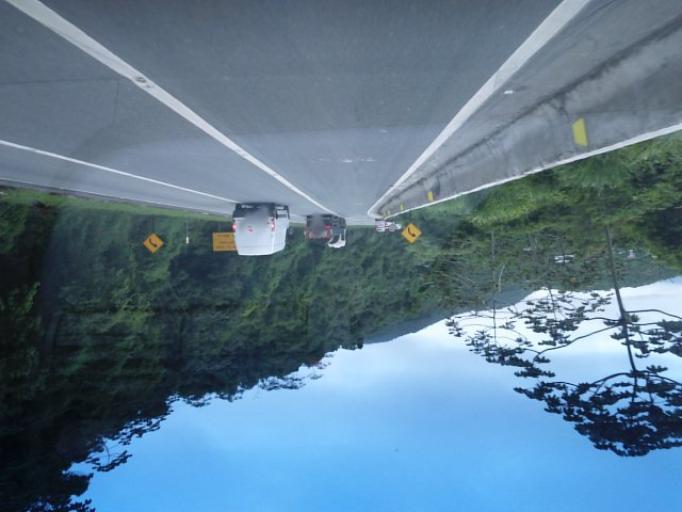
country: BR
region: Santa Catarina
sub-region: Itapema
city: Itapema
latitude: -27.0529
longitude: -48.6001
